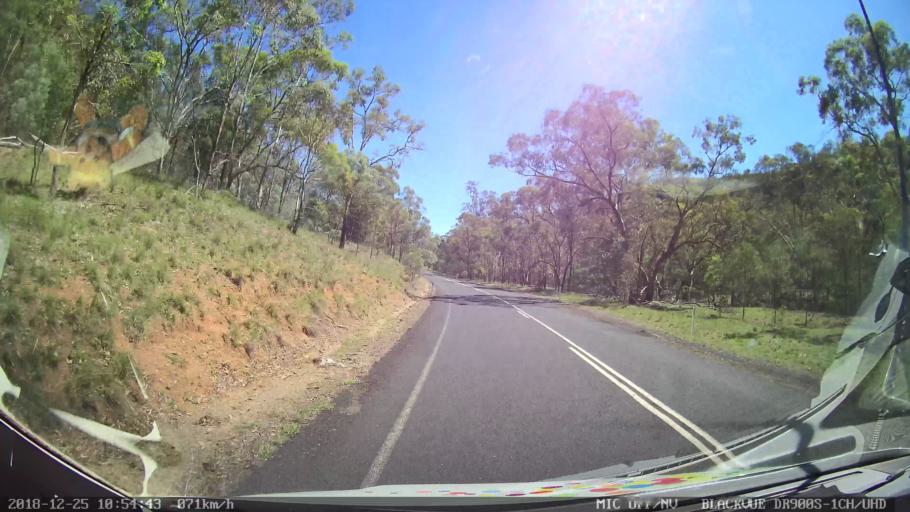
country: AU
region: New South Wales
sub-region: Upper Hunter Shire
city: Merriwa
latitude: -32.4069
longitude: 150.2736
